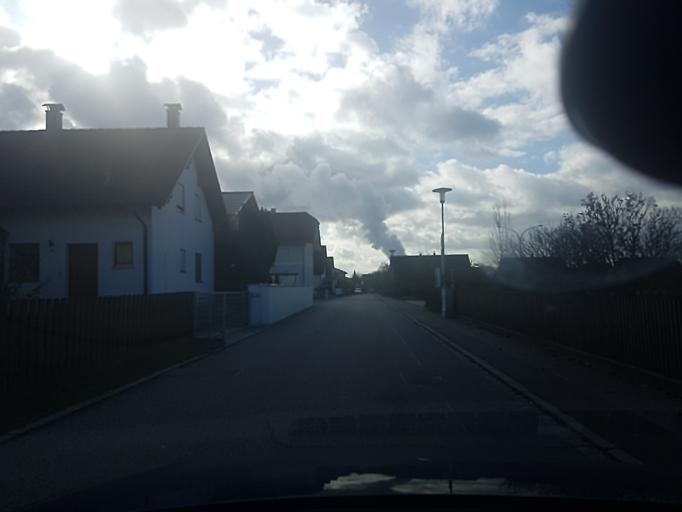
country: DE
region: Bavaria
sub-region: Lower Bavaria
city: Worth an der Isar
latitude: 48.6215
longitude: 12.3349
